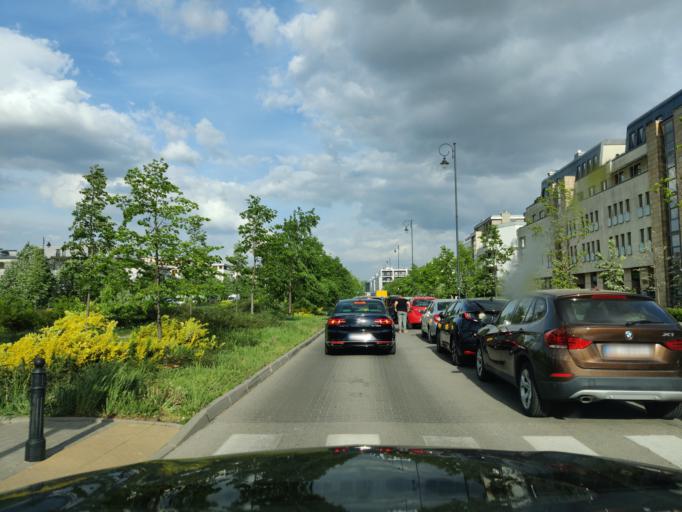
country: PL
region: Masovian Voivodeship
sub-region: Warszawa
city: Wilanow
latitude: 52.1647
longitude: 21.0746
